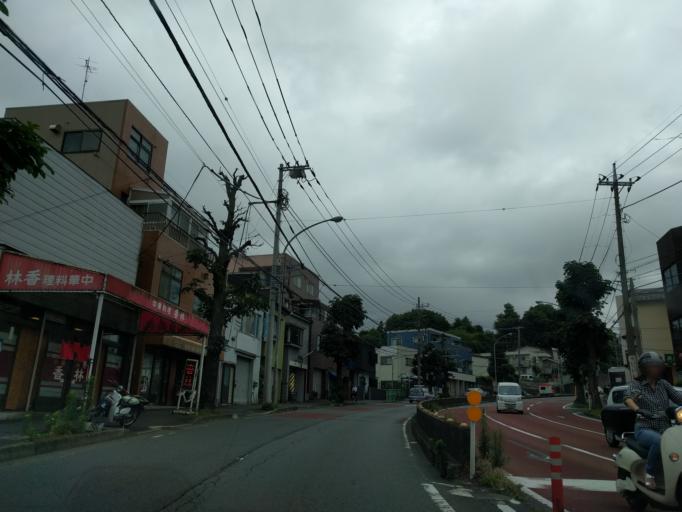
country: JP
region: Kanagawa
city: Yokohama
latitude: 35.4380
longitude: 139.5964
